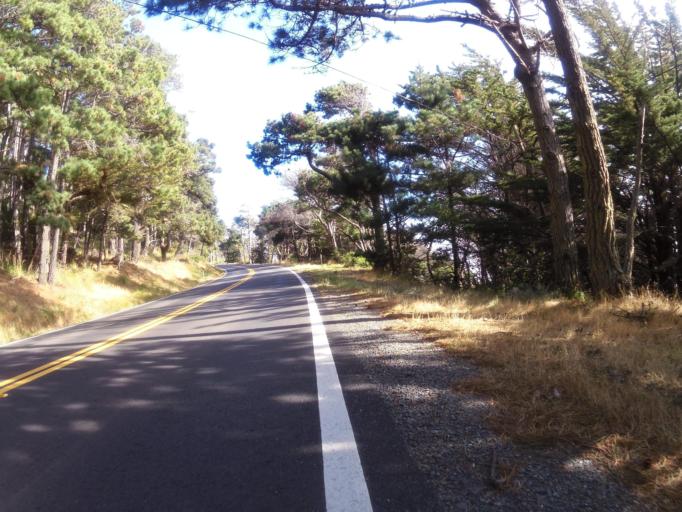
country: US
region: California
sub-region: Sonoma County
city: Sea Ranch
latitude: 38.8331
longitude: -123.6252
